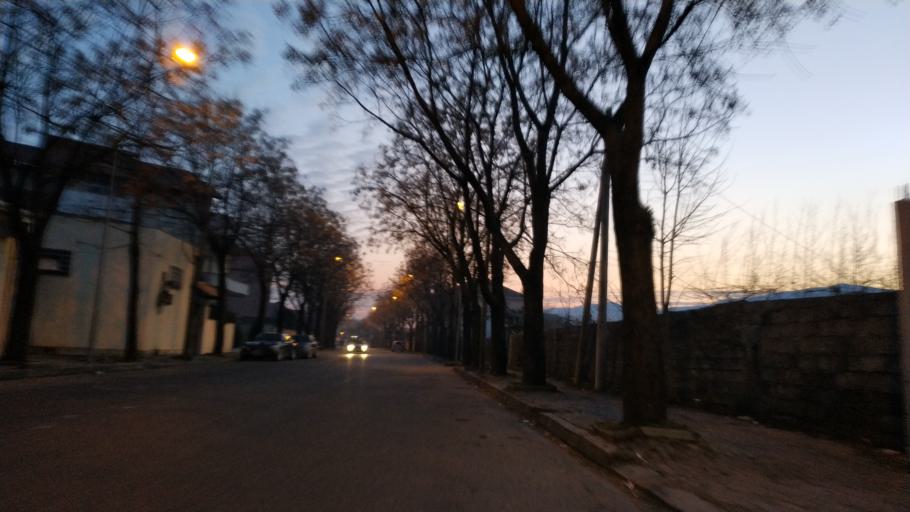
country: AL
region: Shkoder
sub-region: Rrethi i Shkodres
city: Shkoder
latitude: 42.0757
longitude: 19.5031
